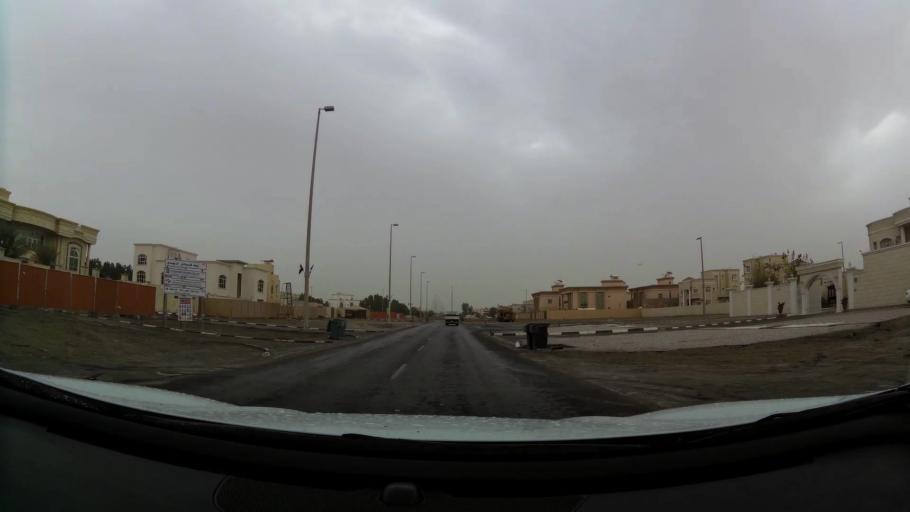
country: AE
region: Abu Dhabi
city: Abu Dhabi
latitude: 24.4166
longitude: 54.5849
